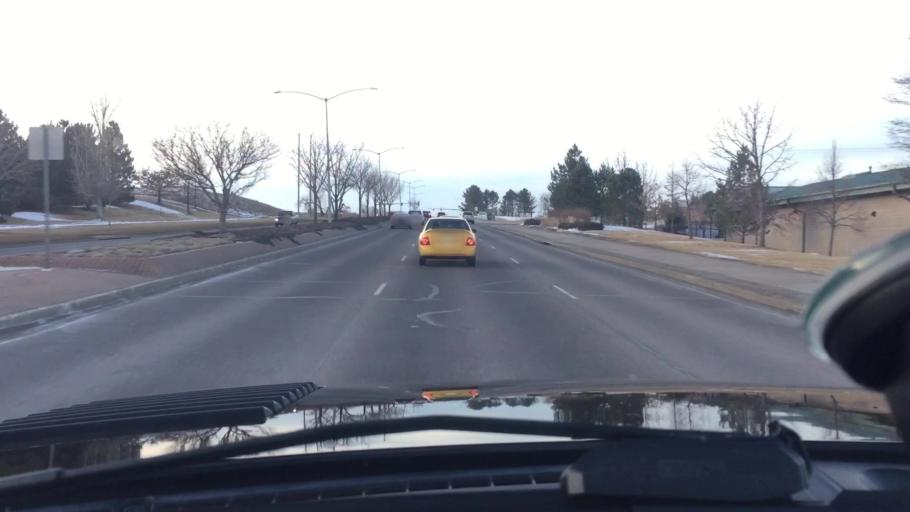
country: US
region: Colorado
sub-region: Broomfield County
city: Broomfield
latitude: 39.8906
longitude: -105.0531
